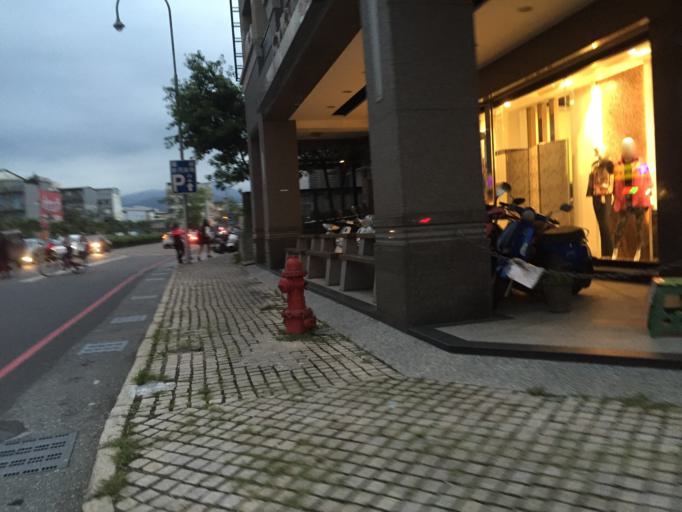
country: TW
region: Taiwan
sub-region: Yilan
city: Yilan
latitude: 24.7531
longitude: 121.7515
